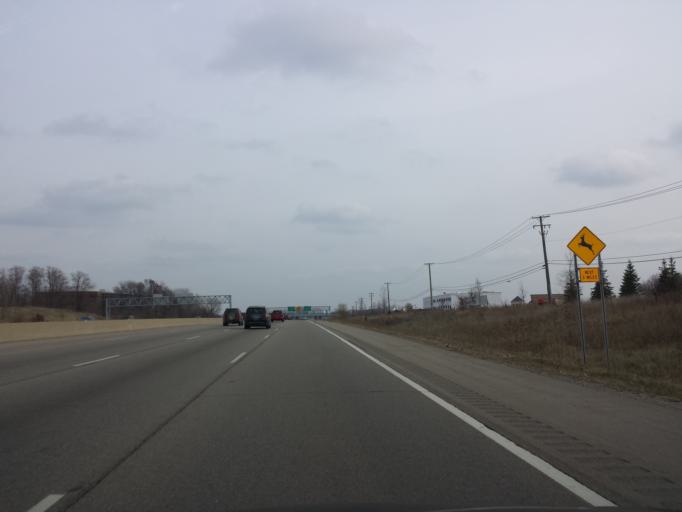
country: US
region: Michigan
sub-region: Oakland County
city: Auburn Hills
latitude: 42.6445
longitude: -83.2057
